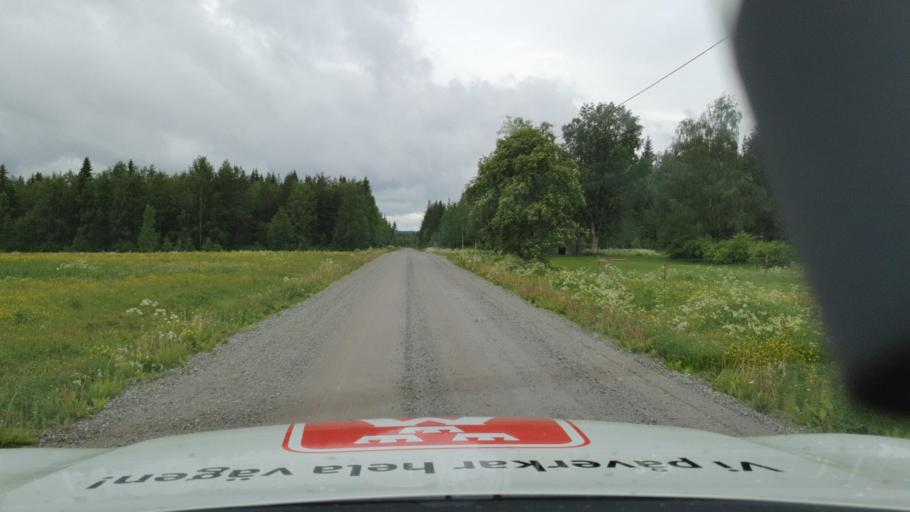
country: SE
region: Vaesterbotten
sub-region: Dorotea Kommun
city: Dorotea
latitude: 64.0834
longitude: 16.6827
